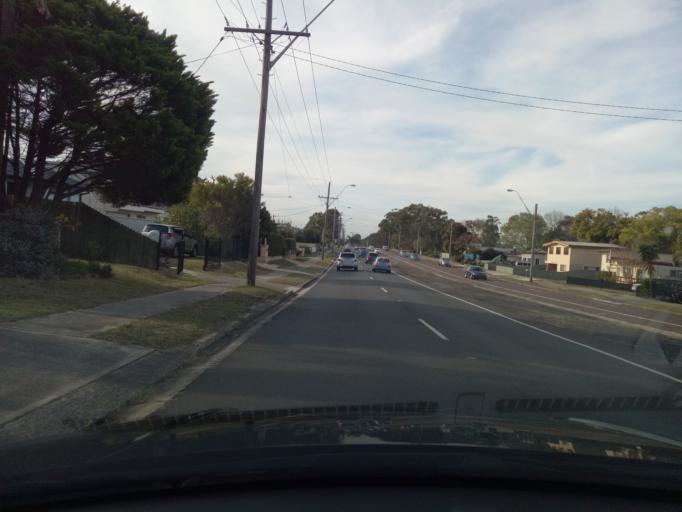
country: AU
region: New South Wales
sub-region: Wyong Shire
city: Bateau Bay
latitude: -33.3844
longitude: 151.4724
